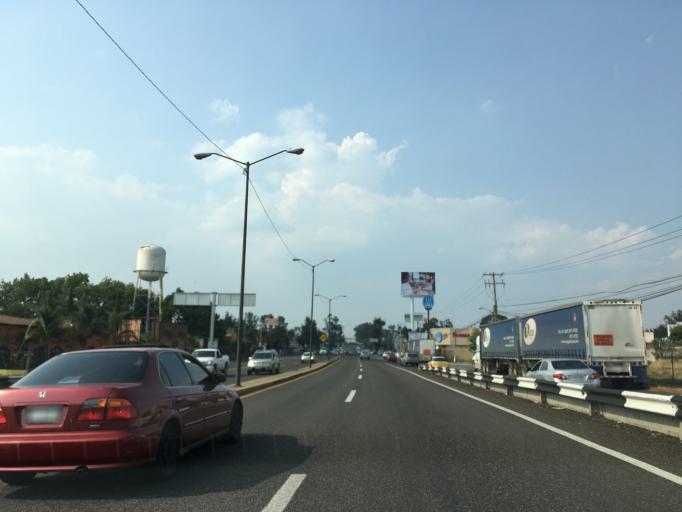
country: MX
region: Michoacan
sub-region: Morelia
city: Morelos
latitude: 19.6670
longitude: -101.2241
